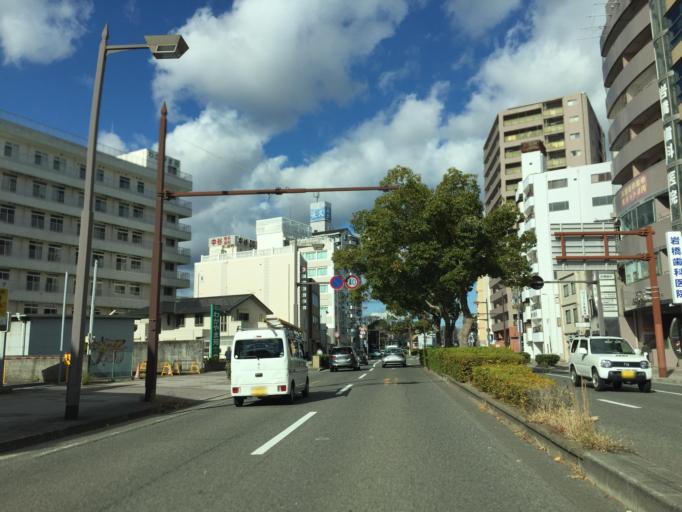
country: JP
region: Wakayama
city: Wakayama-shi
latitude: 34.2305
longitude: 135.1780
